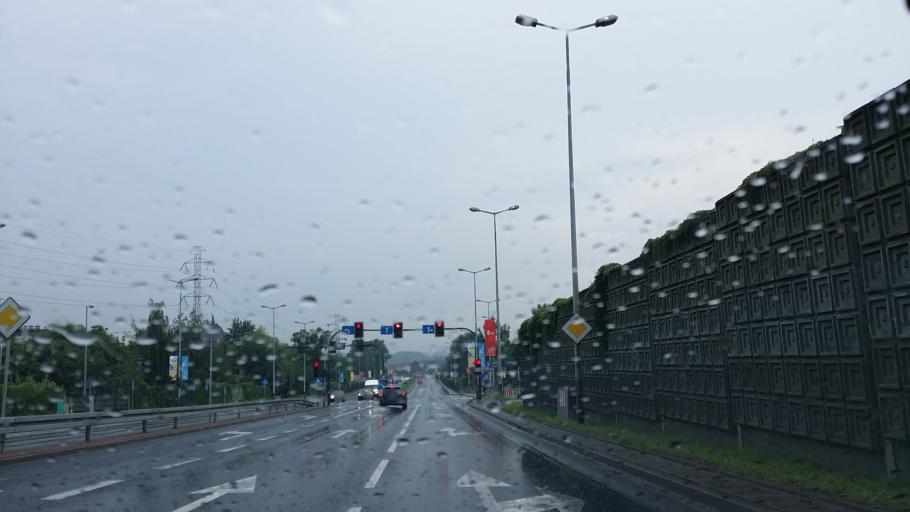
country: PL
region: Lesser Poland Voivodeship
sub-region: Krakow
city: Krakow
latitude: 50.0201
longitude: 19.9456
